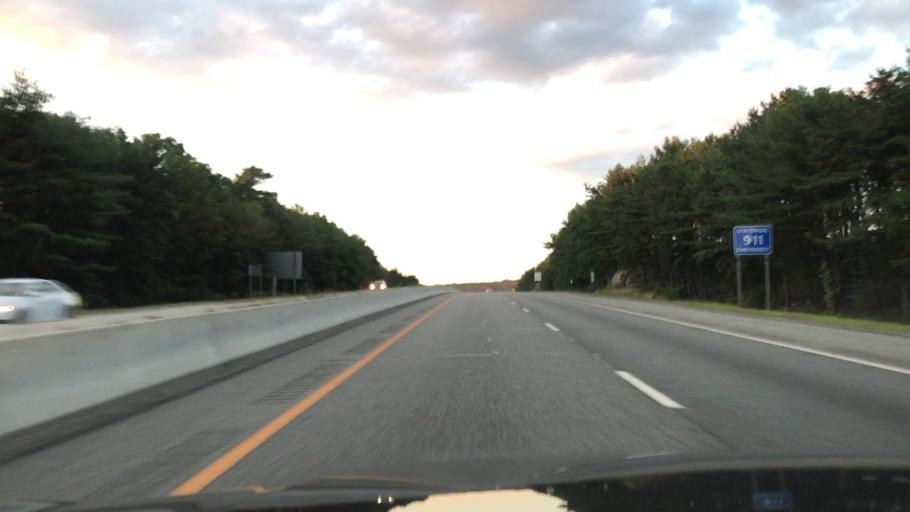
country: US
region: Rhode Island
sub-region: Washington County
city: Hope Valley
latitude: 41.5181
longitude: -71.6886
